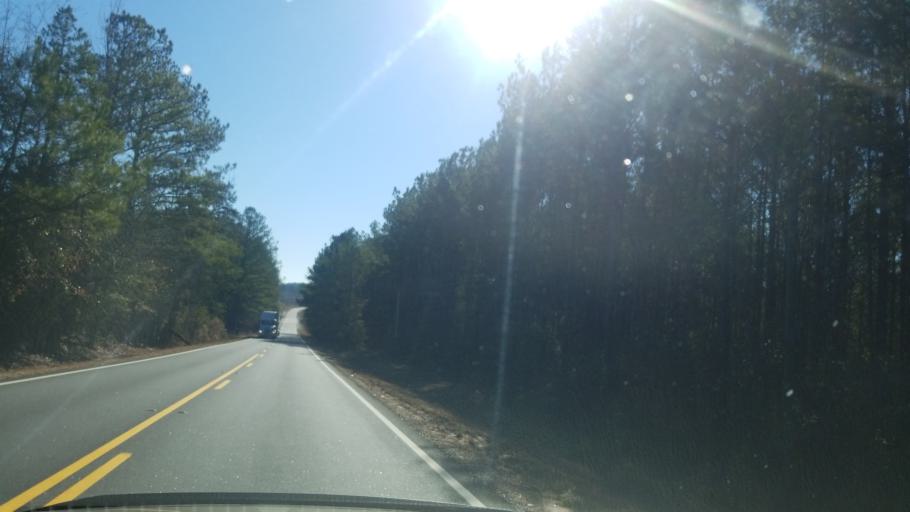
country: US
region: Alabama
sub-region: Chambers County
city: Valley
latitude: 32.8404
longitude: -85.1199
